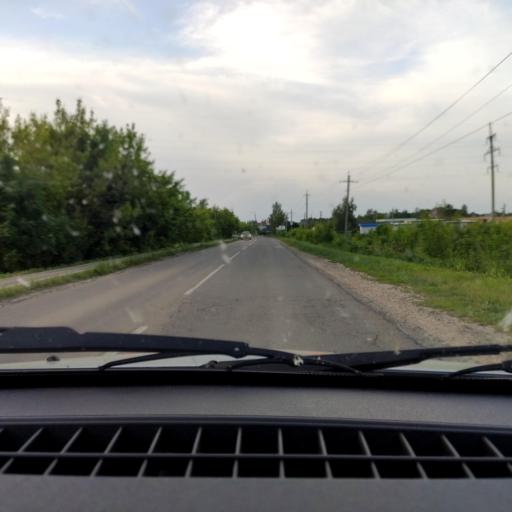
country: RU
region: Voronezj
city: Ramon'
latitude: 51.9488
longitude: 39.3557
